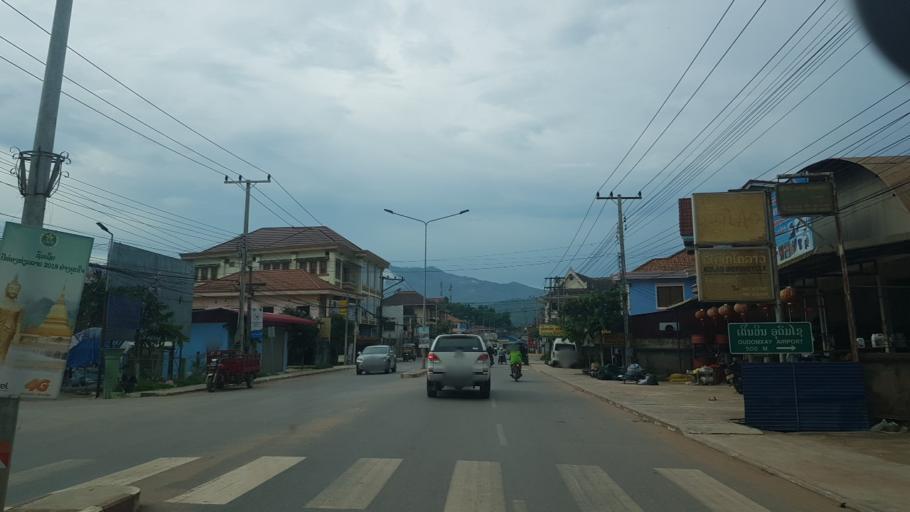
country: LA
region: Oudomxai
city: Muang Xay
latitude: 20.6825
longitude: 101.9867
